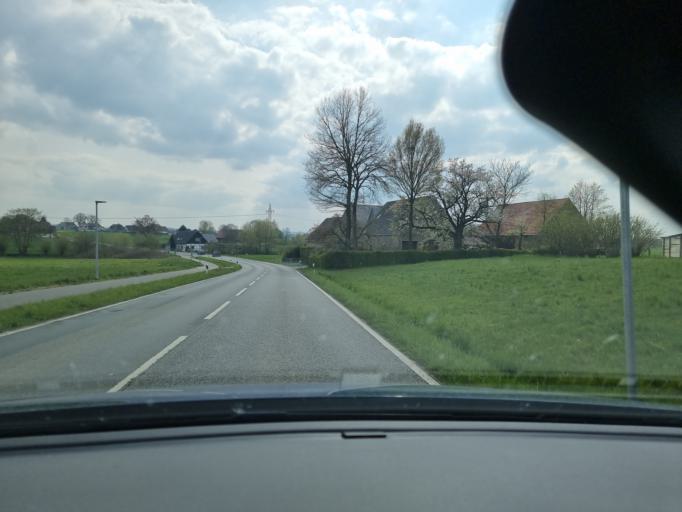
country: DE
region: North Rhine-Westphalia
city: Spenge
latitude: 52.1574
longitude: 8.4967
